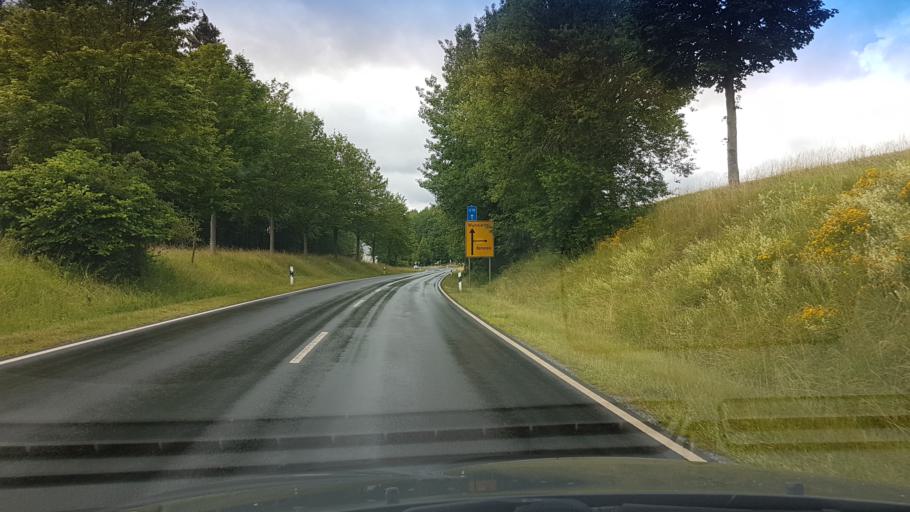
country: DE
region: Bavaria
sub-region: Upper Franconia
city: Wunsiedel
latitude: 50.0550
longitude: 12.0501
